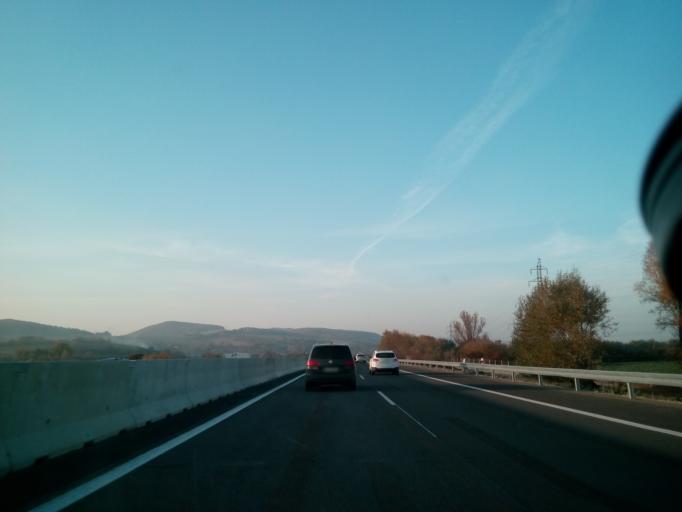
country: SK
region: Presovsky
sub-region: Okres Presov
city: Presov
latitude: 48.8653
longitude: 21.2593
